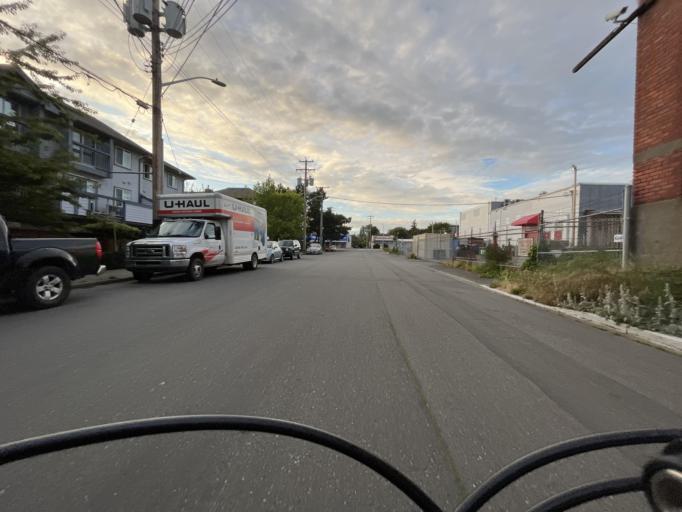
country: CA
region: British Columbia
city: Victoria
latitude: 48.4296
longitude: -123.3871
